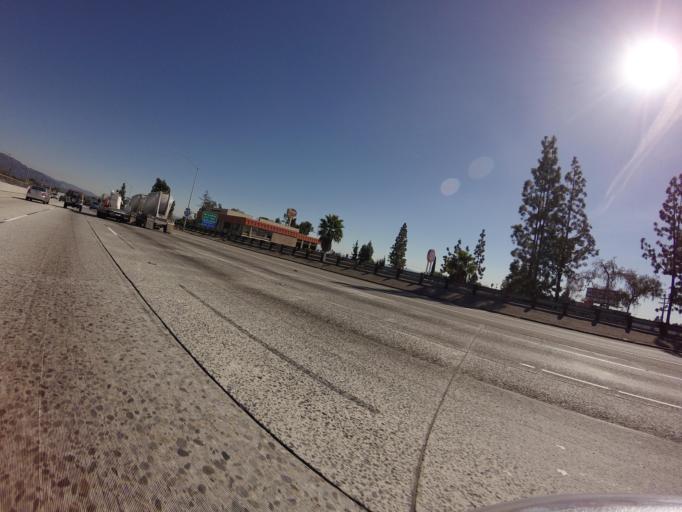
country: US
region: California
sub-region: Los Angeles County
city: Monrovia
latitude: 34.1354
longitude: -118.0024
